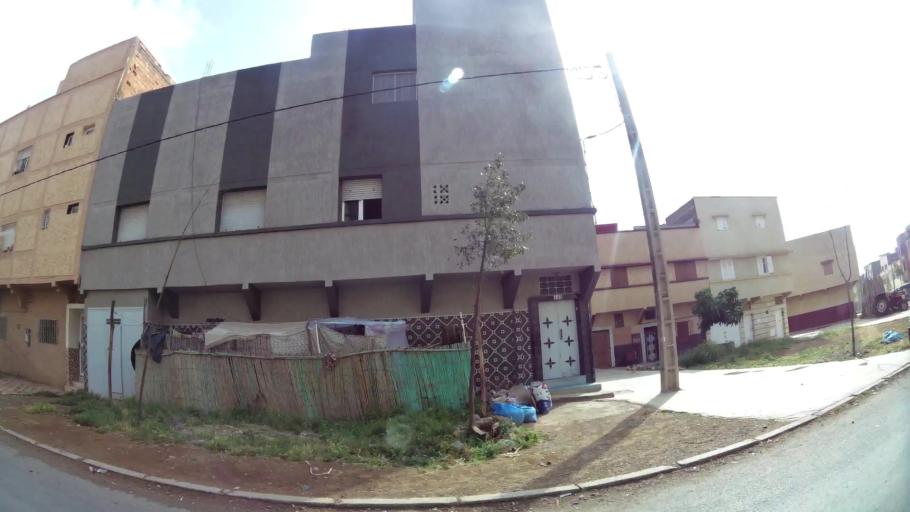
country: MA
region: Rabat-Sale-Zemmour-Zaer
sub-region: Khemisset
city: Tiflet
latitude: 33.8857
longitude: -6.3148
